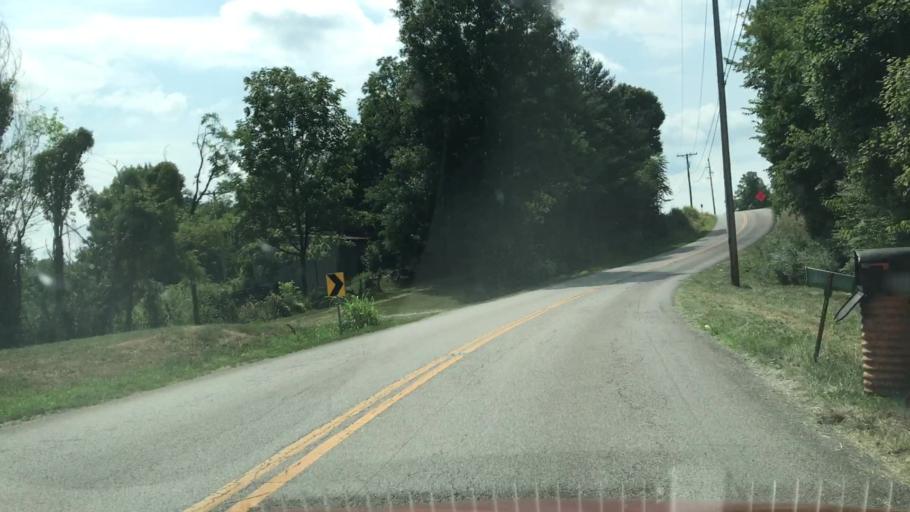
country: US
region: Kentucky
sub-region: Barren County
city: Glasgow
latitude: 36.8988
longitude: -85.8598
